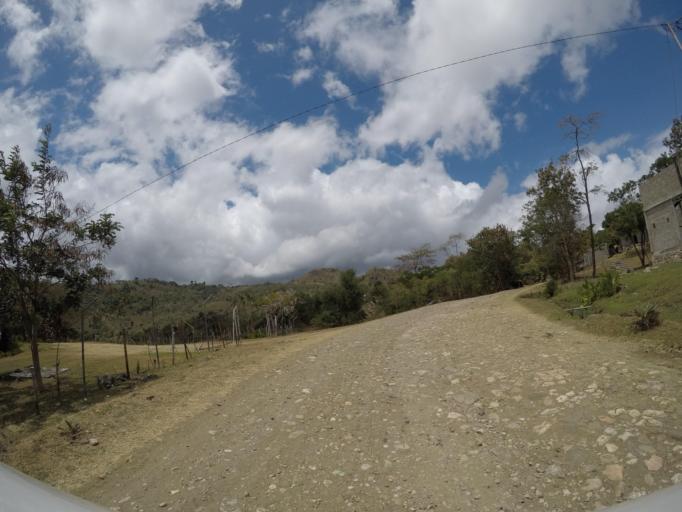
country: TL
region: Lautem
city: Lospalos
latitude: -8.5441
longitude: 126.8360
